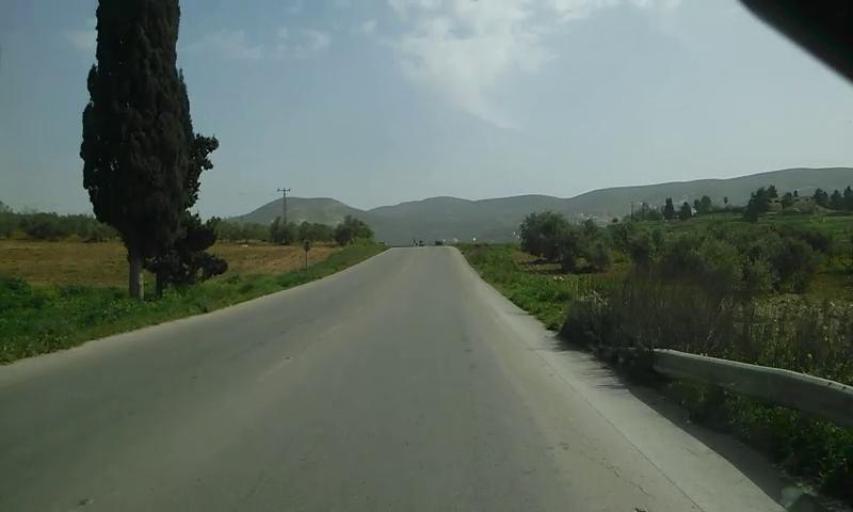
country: PS
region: West Bank
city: Al Fandaqumiyah
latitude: 32.3410
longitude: 35.2029
